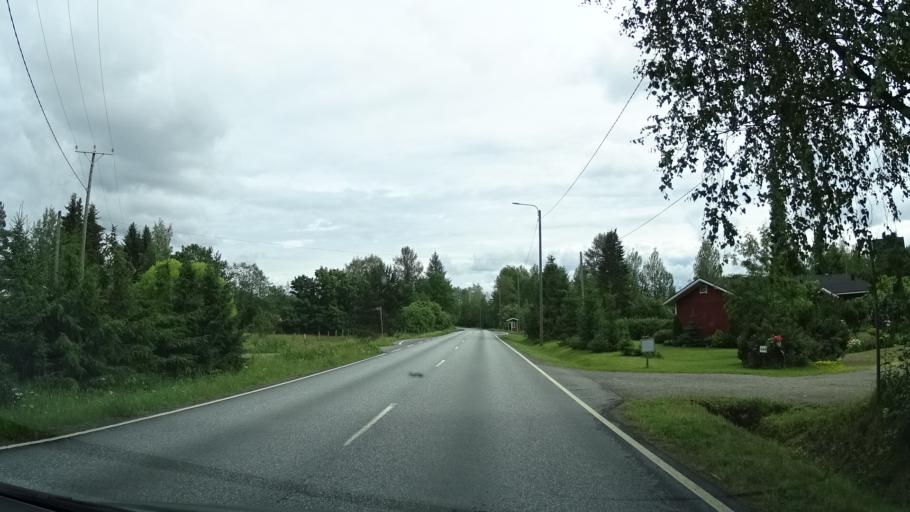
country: FI
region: Pirkanmaa
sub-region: Etelae-Pirkanmaa
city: Urjala
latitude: 61.0831
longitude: 23.4274
